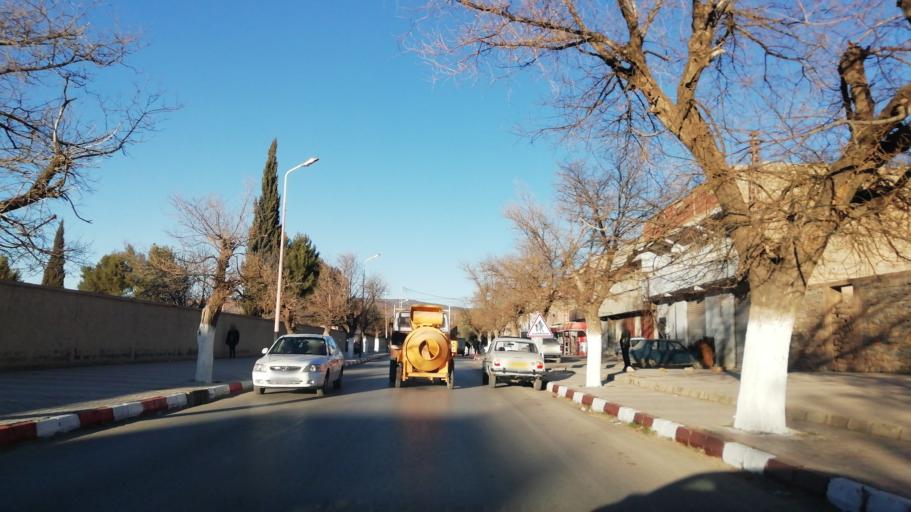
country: DZ
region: Tlemcen
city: Sebdou
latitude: 34.6486
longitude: -1.3210
